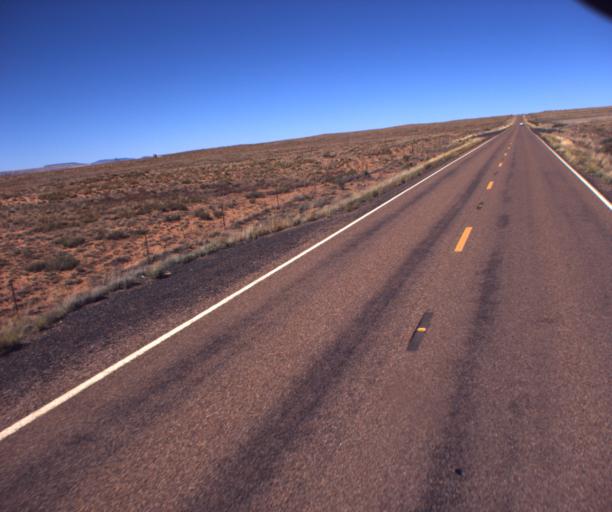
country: US
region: Arizona
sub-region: Navajo County
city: Holbrook
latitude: 34.9912
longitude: -110.0891
